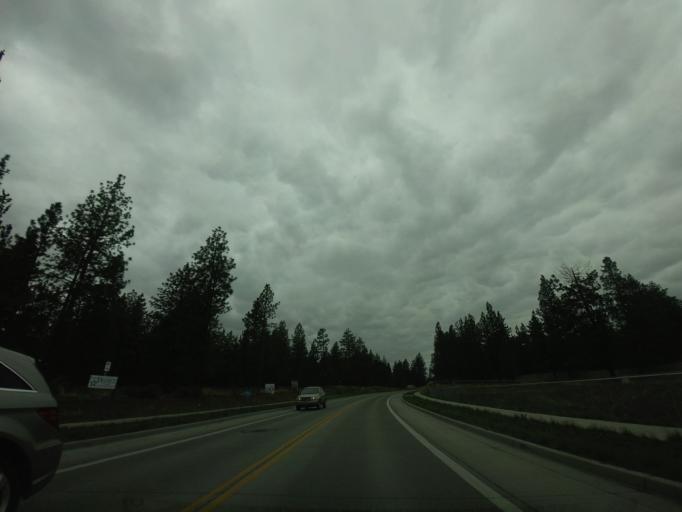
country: US
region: Oregon
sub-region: Deschutes County
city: Bend
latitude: 44.0185
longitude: -121.3222
